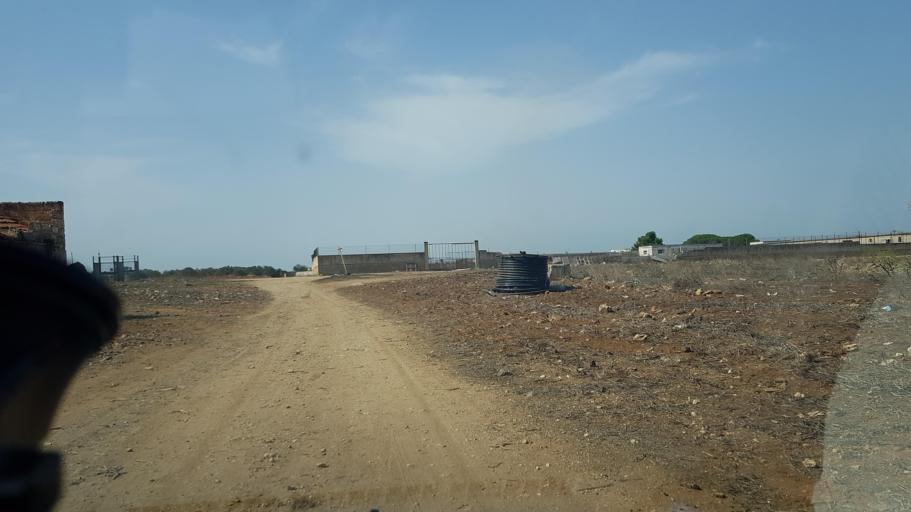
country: IT
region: Apulia
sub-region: Provincia di Brindisi
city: Brindisi
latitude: 40.5945
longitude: 17.8763
